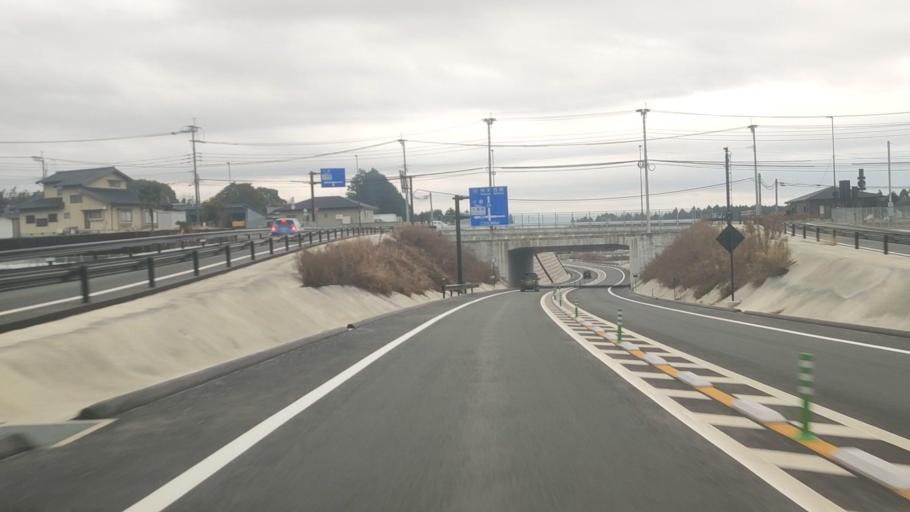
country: JP
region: Kumamoto
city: Ozu
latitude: 32.8911
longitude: 130.8964
